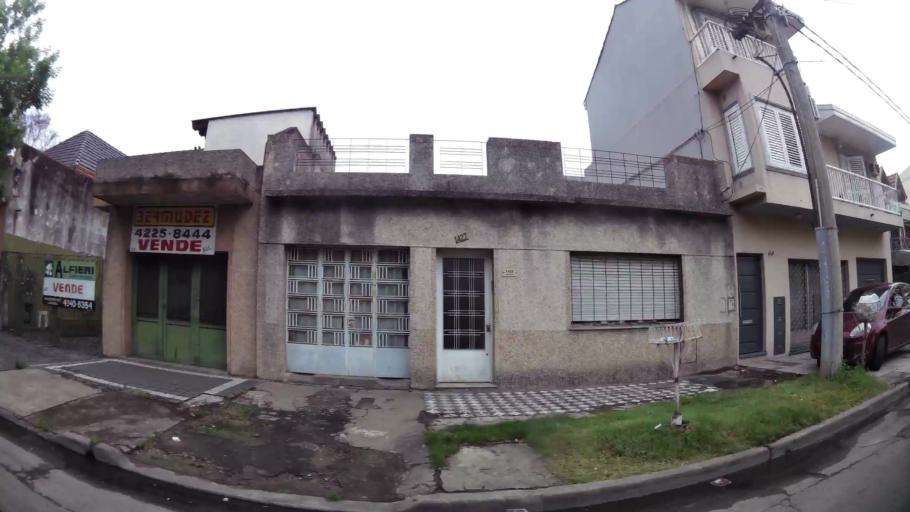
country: AR
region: Buenos Aires
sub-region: Partido de Lanus
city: Lanus
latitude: -34.7059
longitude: -58.3818
